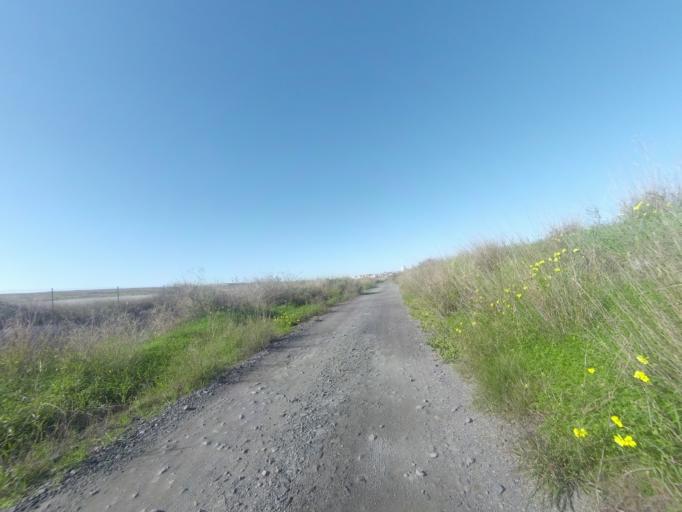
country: ES
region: Andalusia
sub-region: Provincia de Huelva
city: Palos de la Frontera
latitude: 37.2525
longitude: -6.9047
